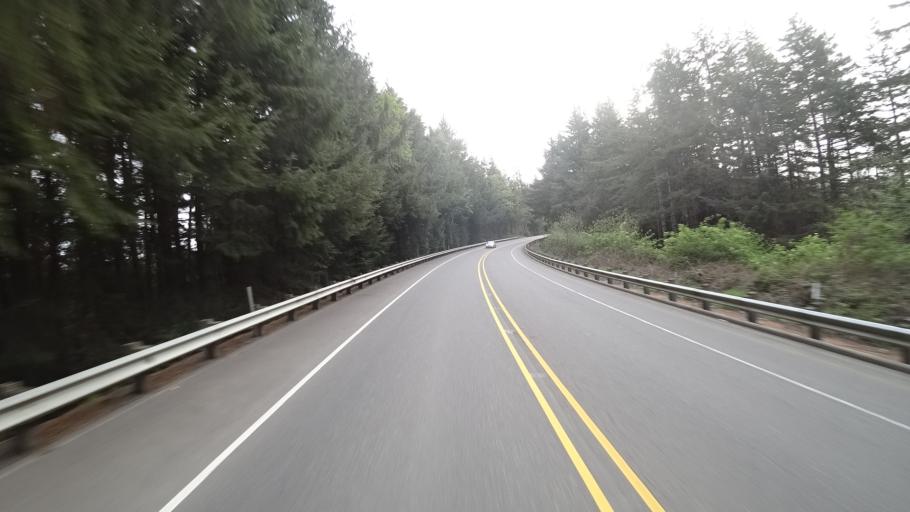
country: US
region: Oregon
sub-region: Coos County
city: Barview
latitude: 43.2548
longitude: -124.2843
